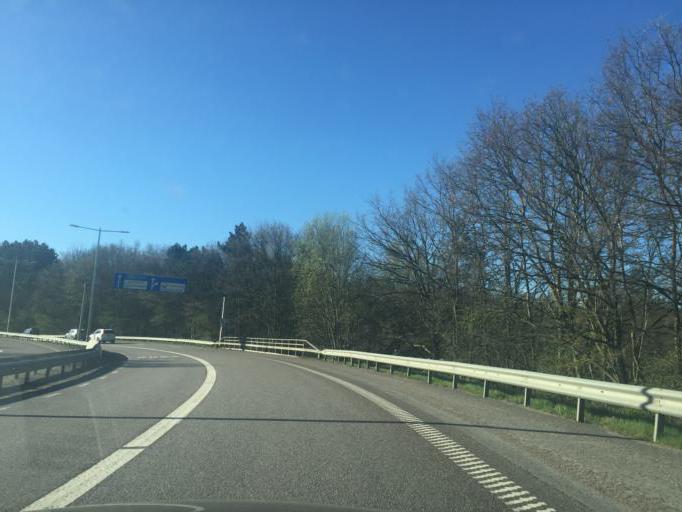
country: SE
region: Vaestra Goetaland
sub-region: Goteborg
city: Majorna
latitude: 57.6857
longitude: 11.9003
